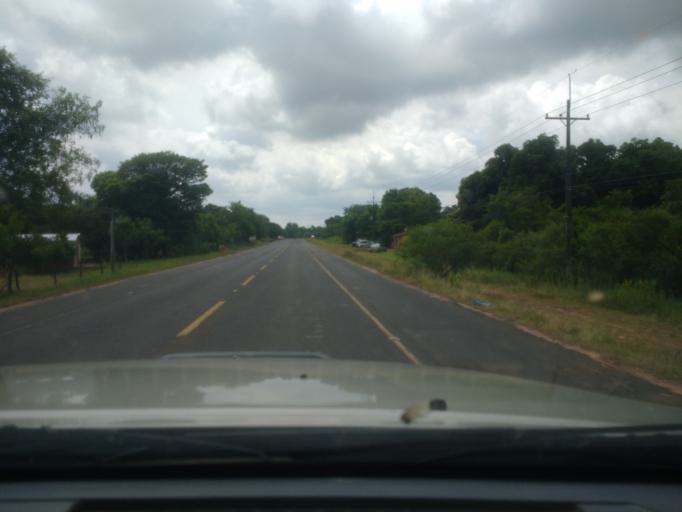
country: PY
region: San Pedro
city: Puerto Rosario
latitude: -24.4181
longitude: -57.0994
